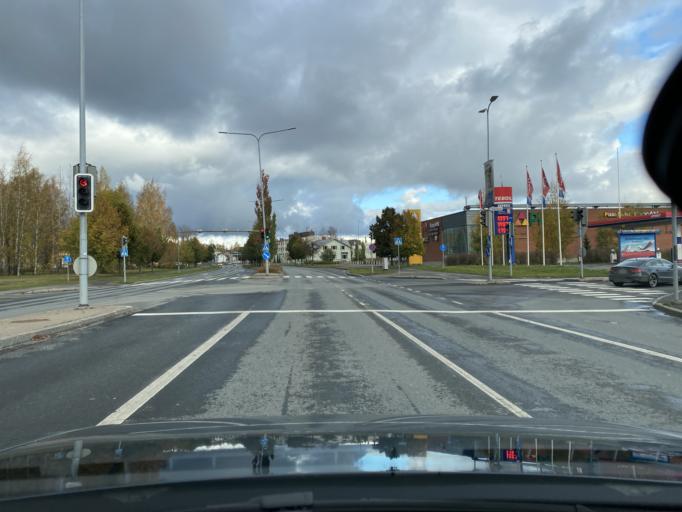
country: FI
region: Haeme
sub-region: Forssa
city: Forssa
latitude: 60.8115
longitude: 23.6317
